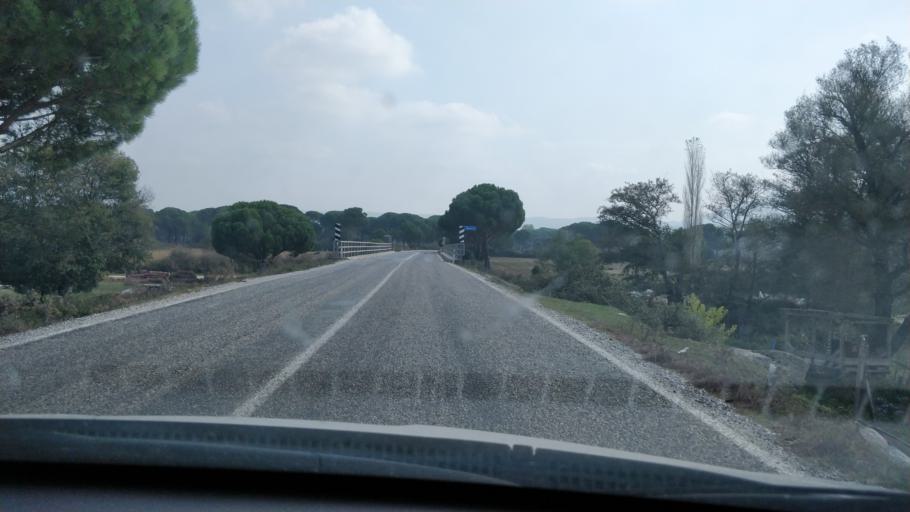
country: TR
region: Izmir
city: Kozak
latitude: 39.2610
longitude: 27.0330
